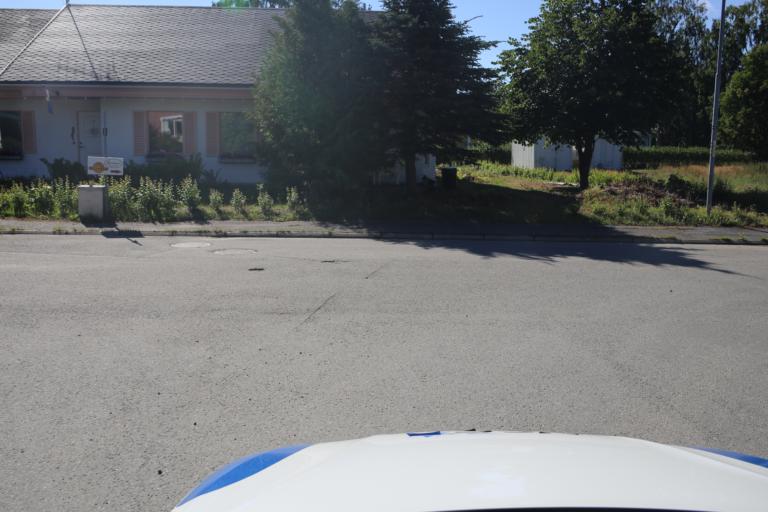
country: SE
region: Vaesterbotten
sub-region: Skelleftea Kommun
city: Viken
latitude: 64.7454
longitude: 20.7681
